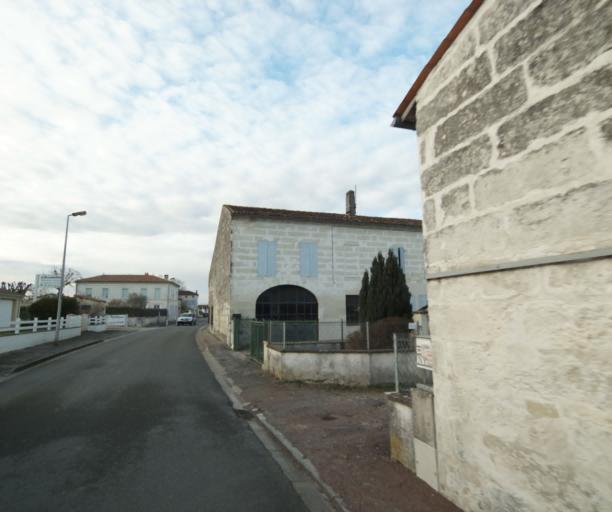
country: FR
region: Poitou-Charentes
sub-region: Departement de la Charente-Maritime
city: Les Gonds
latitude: 45.7140
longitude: -0.6137
